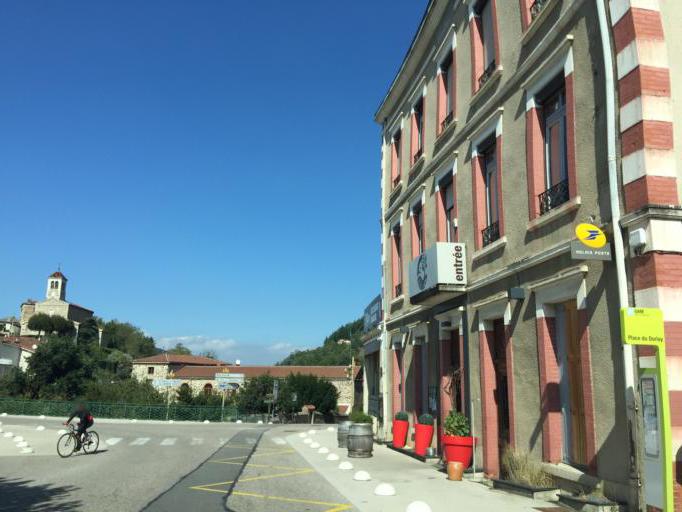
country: FR
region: Rhone-Alpes
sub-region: Departement de la Loire
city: Saint-Paul-en-Jarez
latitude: 45.4469
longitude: 4.5835
